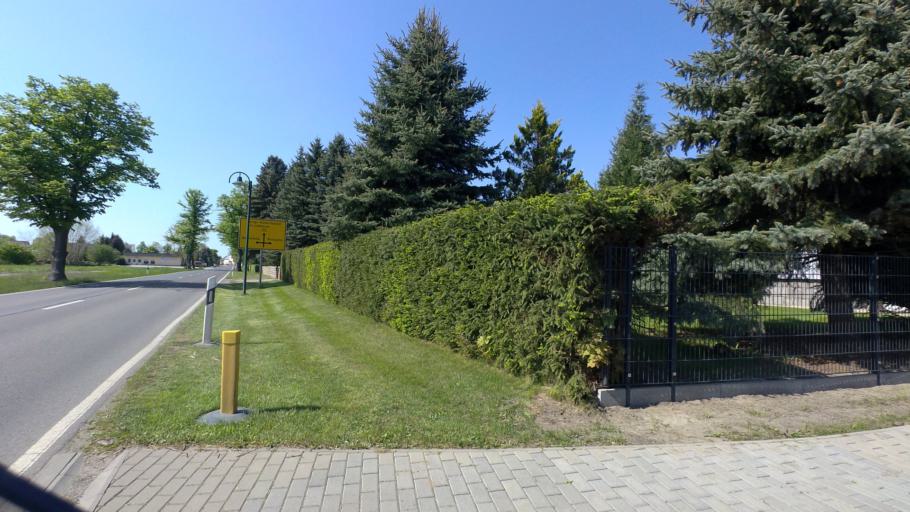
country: DE
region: Brandenburg
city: Schlepzig
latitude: 52.0572
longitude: 13.9620
